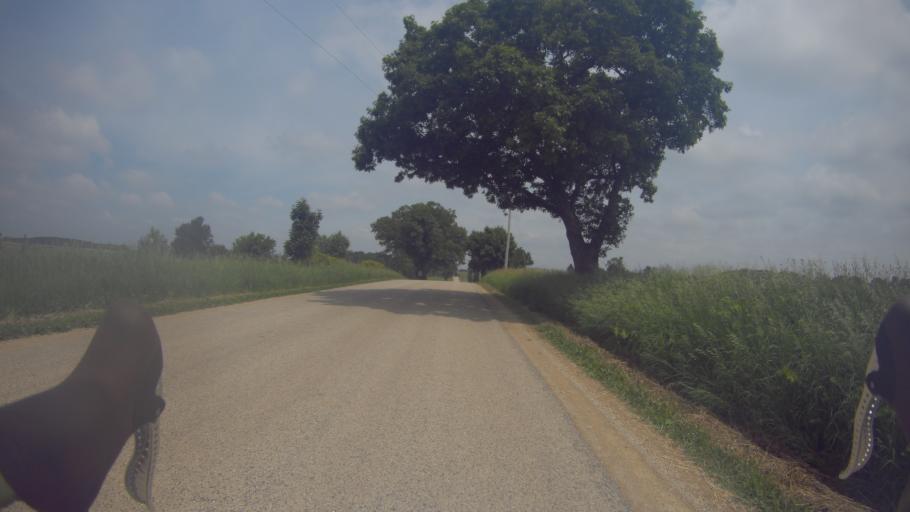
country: US
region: Wisconsin
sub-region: Jefferson County
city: Lake Ripley
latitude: 42.9779
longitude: -88.9987
